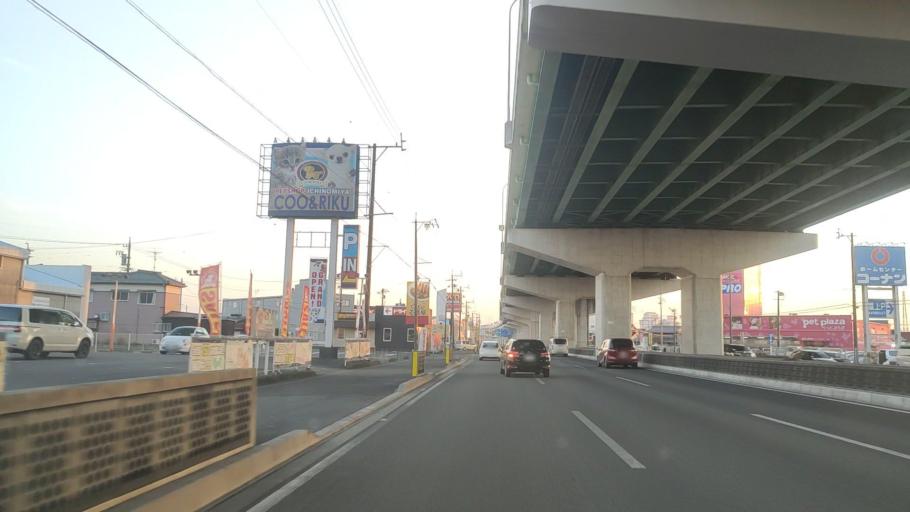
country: JP
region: Aichi
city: Ichinomiya
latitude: 35.2811
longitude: 136.8302
